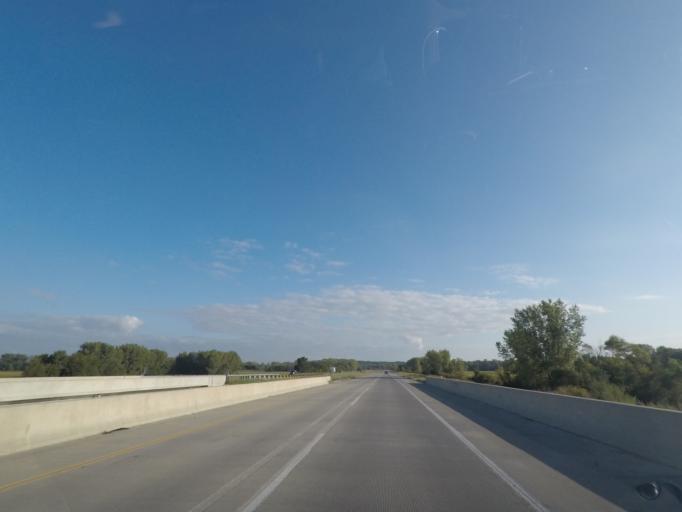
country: US
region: Iowa
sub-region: Polk County
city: Pleasant Hill
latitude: 41.5464
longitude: -93.5139
